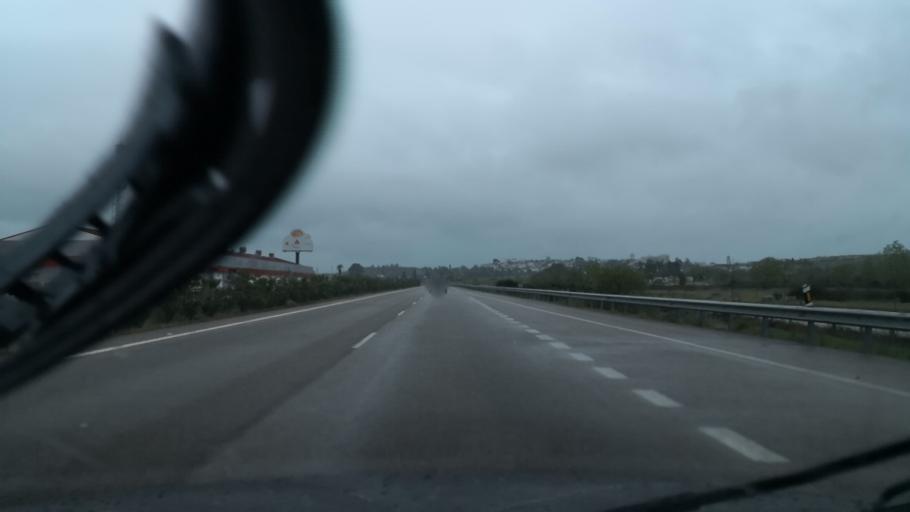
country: ES
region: Extremadura
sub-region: Provincia de Badajoz
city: Badajoz
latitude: 38.9050
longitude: -6.9665
